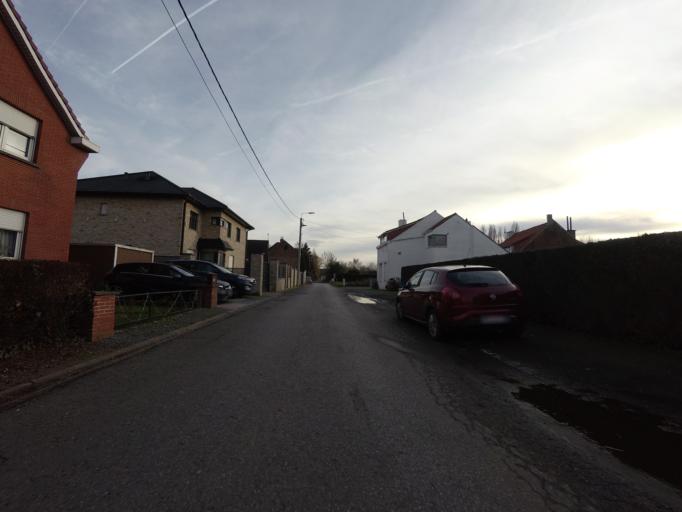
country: BE
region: Flanders
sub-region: Provincie Vlaams-Brabant
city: Kortenberg
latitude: 50.8824
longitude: 4.5196
